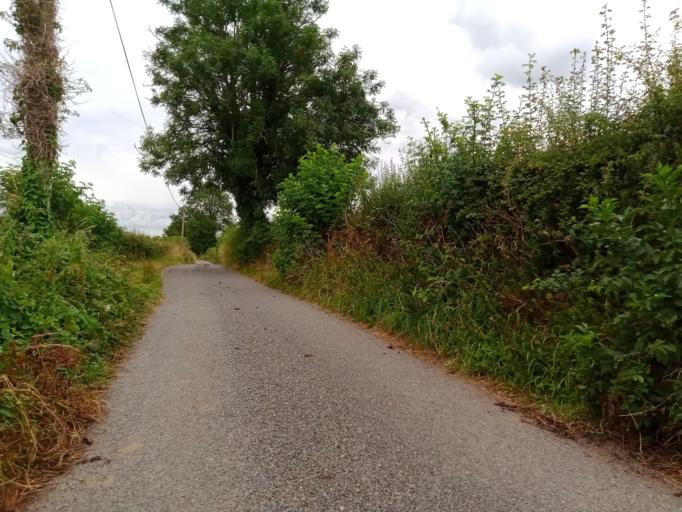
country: IE
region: Leinster
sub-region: Kilkenny
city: Callan
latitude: 52.5432
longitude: -7.4136
